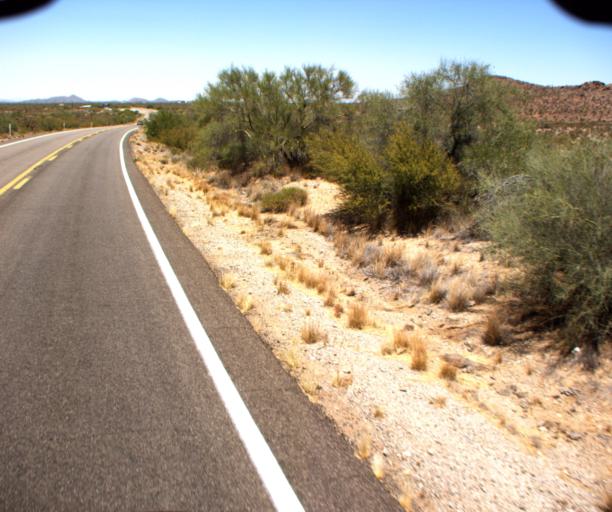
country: US
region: Arizona
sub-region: Pima County
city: Catalina
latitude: 32.6496
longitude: -111.0296
